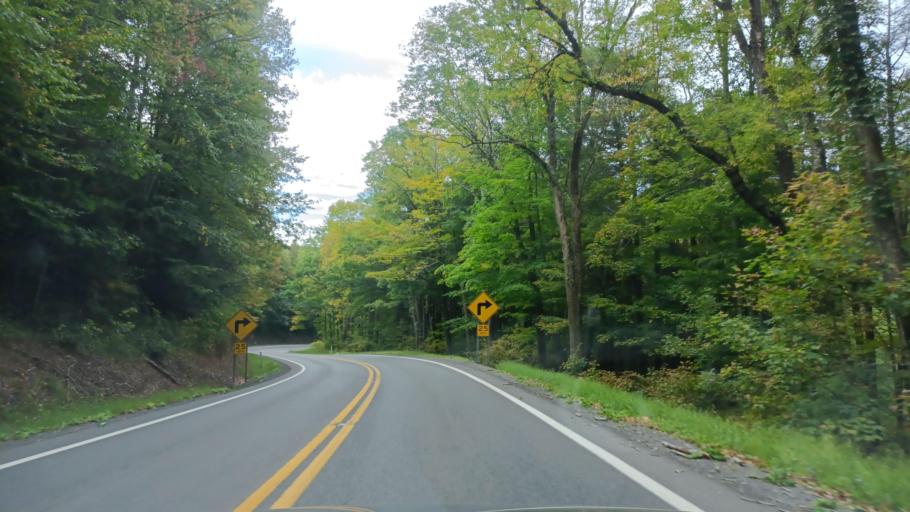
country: US
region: Maryland
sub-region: Garrett County
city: Mountain Lake Park
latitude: 39.2768
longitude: -79.3117
